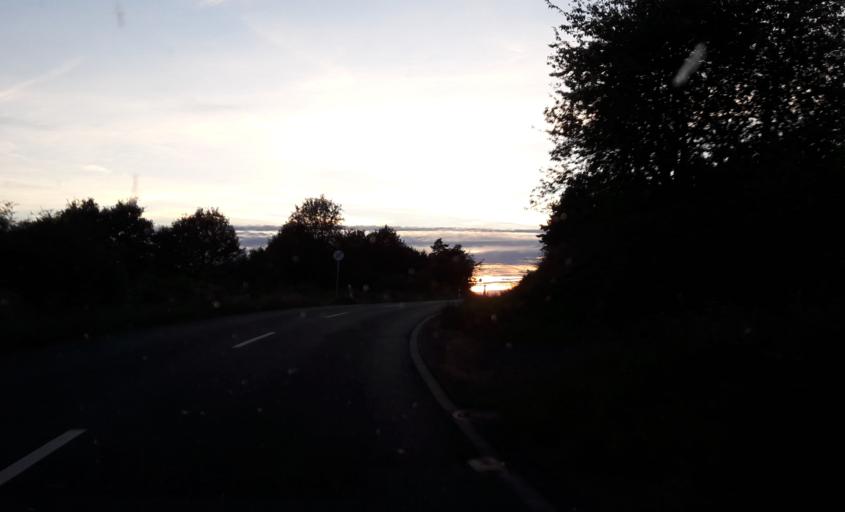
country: DE
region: Rheinland-Pfalz
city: Kinheim
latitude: 49.9881
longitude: 7.0463
